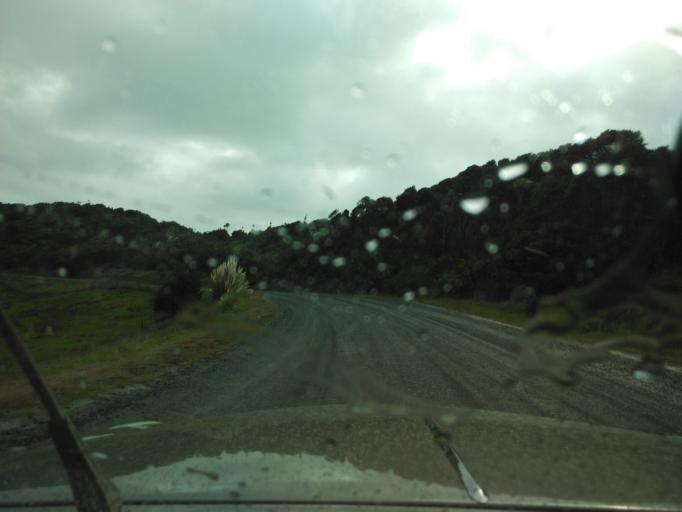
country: NZ
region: Auckland
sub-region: Auckland
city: Wellsford
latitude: -36.3441
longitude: 174.3605
